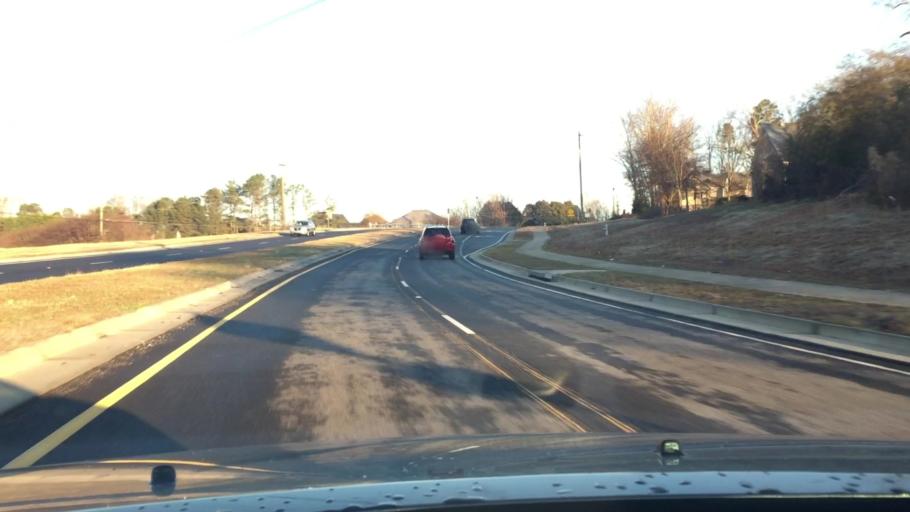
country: US
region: Georgia
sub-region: Forsyth County
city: Cumming
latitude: 34.1862
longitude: -84.1962
